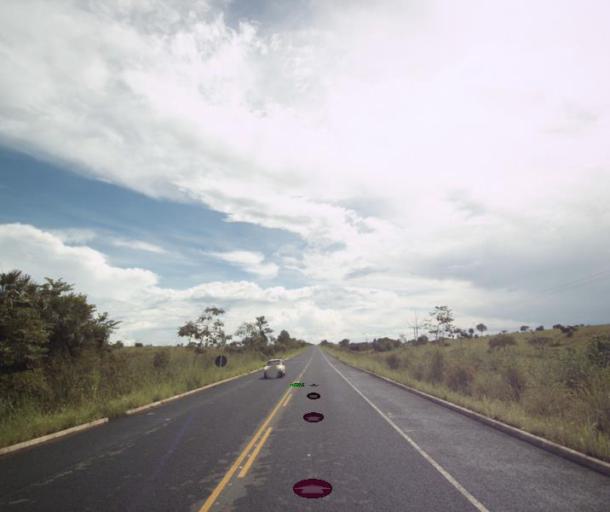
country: BR
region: Goias
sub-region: Sao Miguel Do Araguaia
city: Sao Miguel do Araguaia
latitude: -13.2966
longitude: -50.2406
